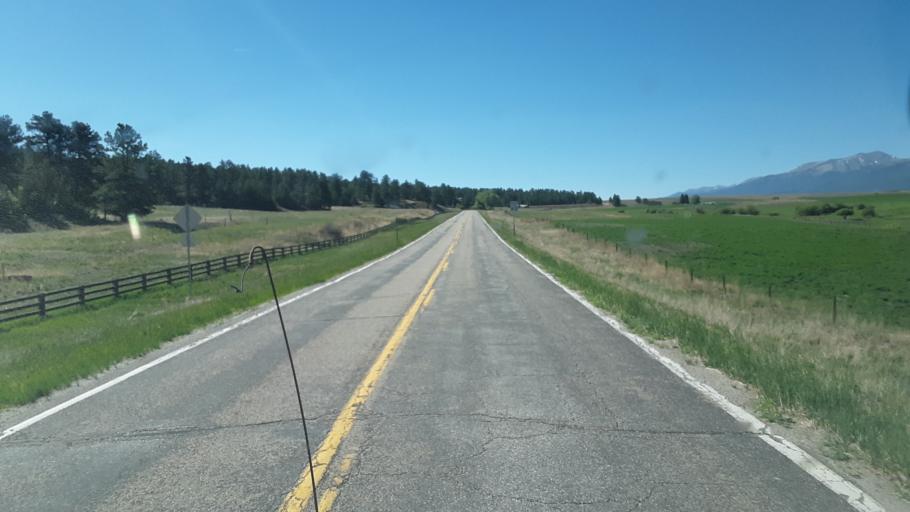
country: US
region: Colorado
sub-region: Custer County
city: Westcliffe
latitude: 38.2275
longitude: -105.5547
